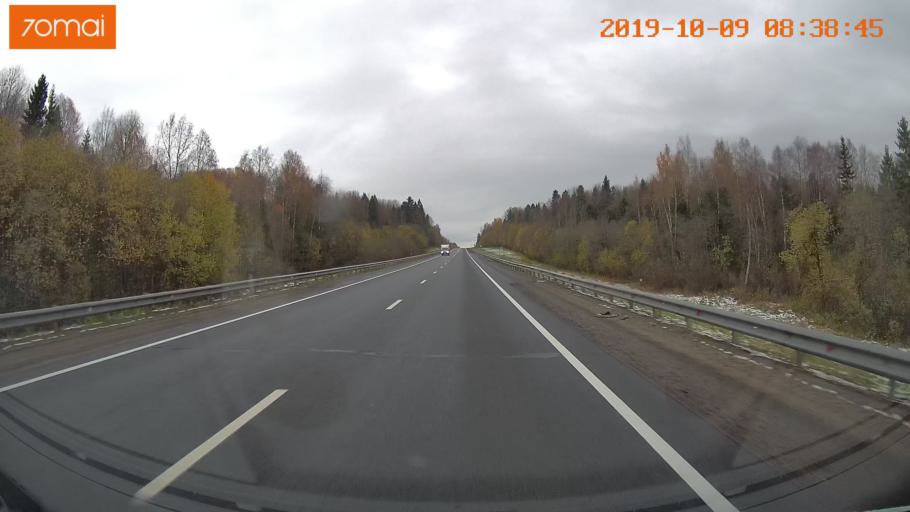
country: RU
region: Vologda
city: Gryazovets
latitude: 58.9612
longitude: 40.1617
